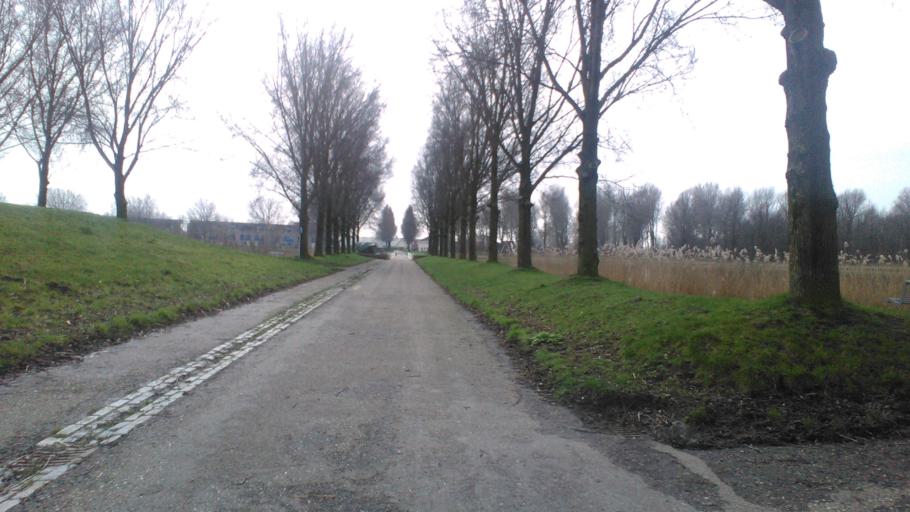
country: NL
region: South Holland
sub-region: Gemeente Pijnacker-Nootdorp
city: Pijnacker
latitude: 52.0424
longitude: 4.4588
